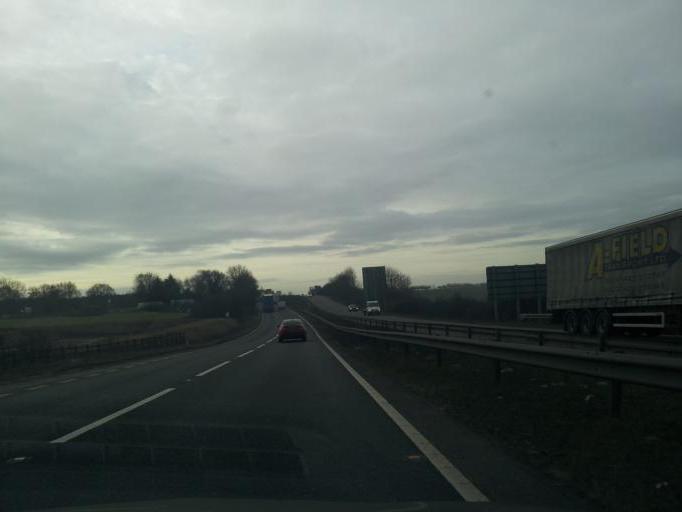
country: GB
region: England
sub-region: District of Rutland
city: Clipsham
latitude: 52.8013
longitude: -0.6106
